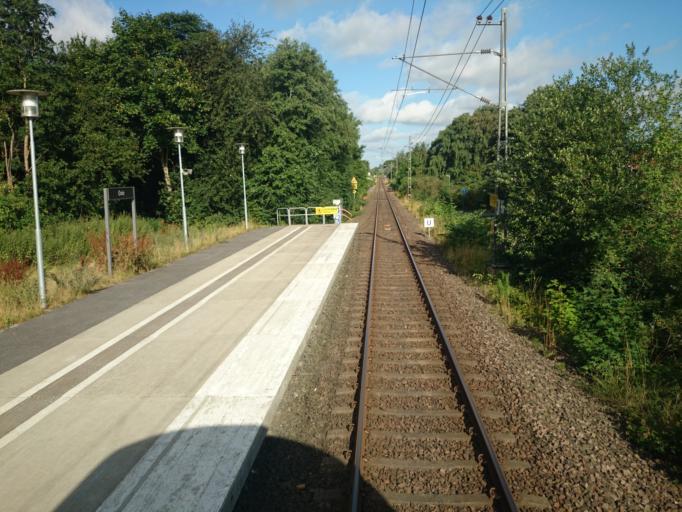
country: SE
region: Skane
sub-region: Malmo
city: Oxie
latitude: 55.5421
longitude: 13.0950
